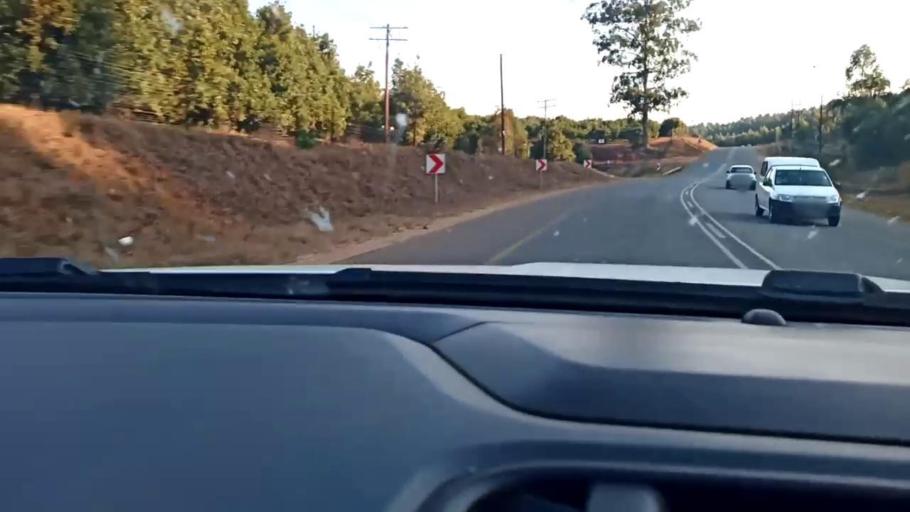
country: ZA
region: Limpopo
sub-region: Mopani District Municipality
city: Duiwelskloof
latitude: -23.7120
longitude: 30.1294
